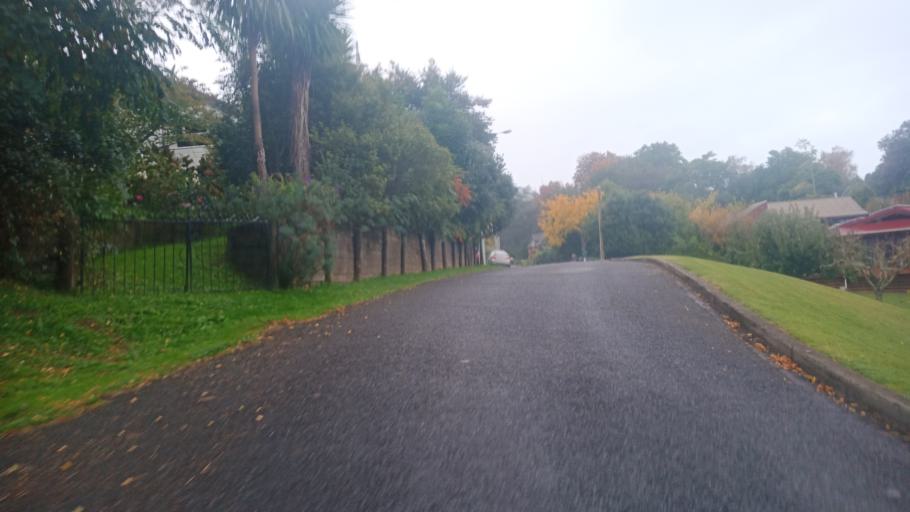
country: NZ
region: Gisborne
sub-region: Gisborne District
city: Gisborne
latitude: -38.6534
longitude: 178.0332
